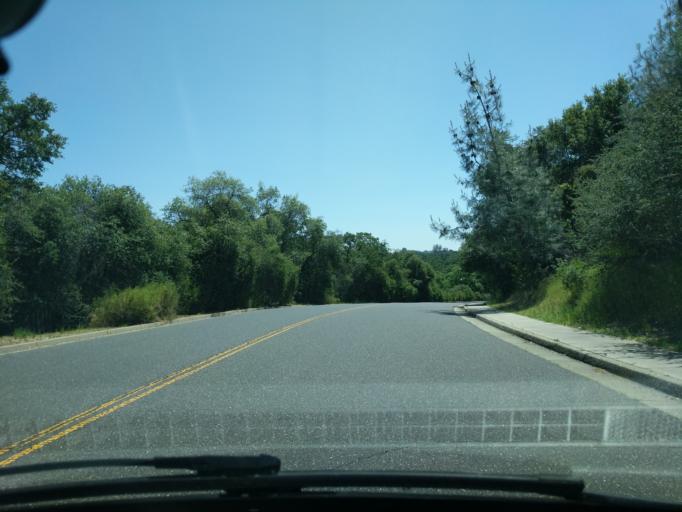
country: US
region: California
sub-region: Calaveras County
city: Angels Camp
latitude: 38.0754
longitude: -120.5625
